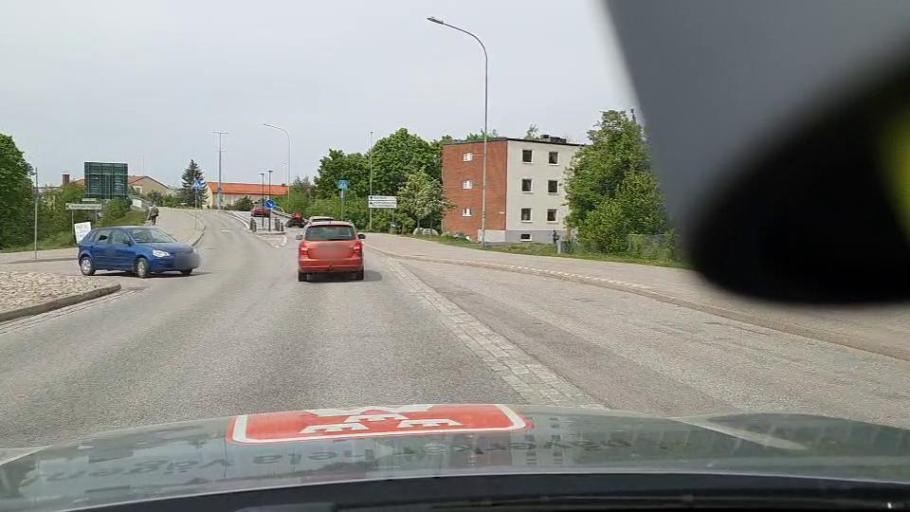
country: SE
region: Soedermanland
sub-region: Flens Kommun
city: Flen
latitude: 59.0521
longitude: 16.5972
